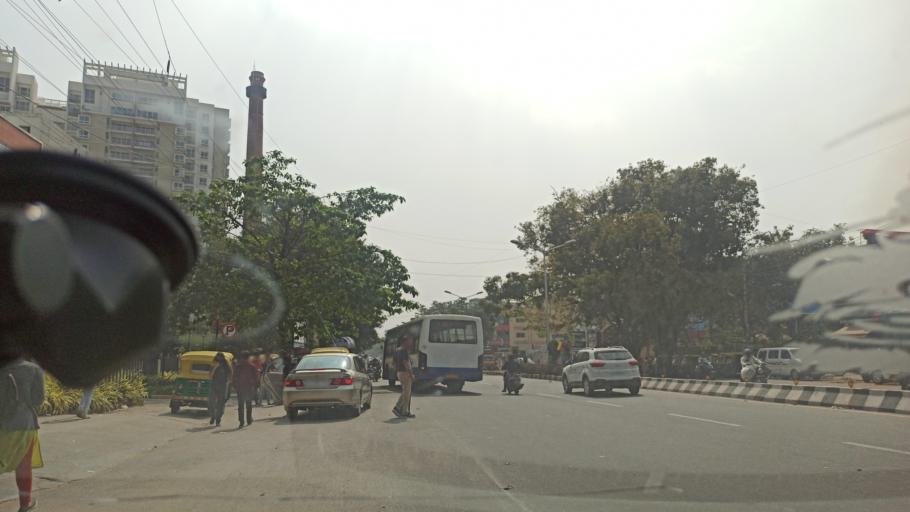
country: IN
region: Karnataka
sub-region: Bangalore Urban
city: Yelahanka
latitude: 13.0949
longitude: 77.5945
